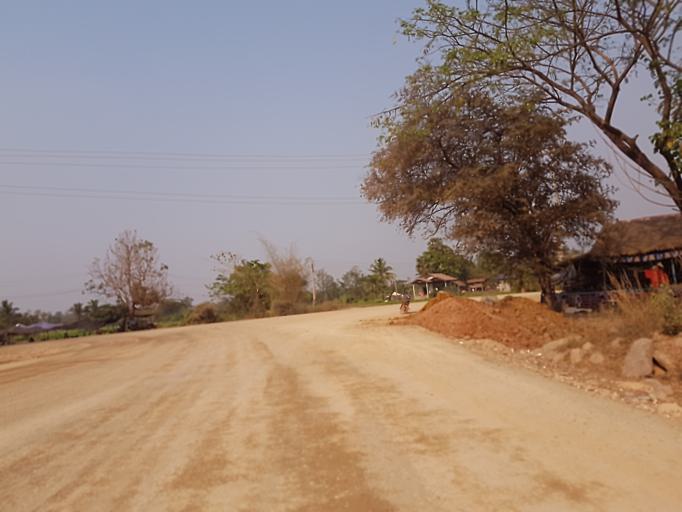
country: TH
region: Nong Khai
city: Phon Phisai
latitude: 17.9999
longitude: 102.9086
